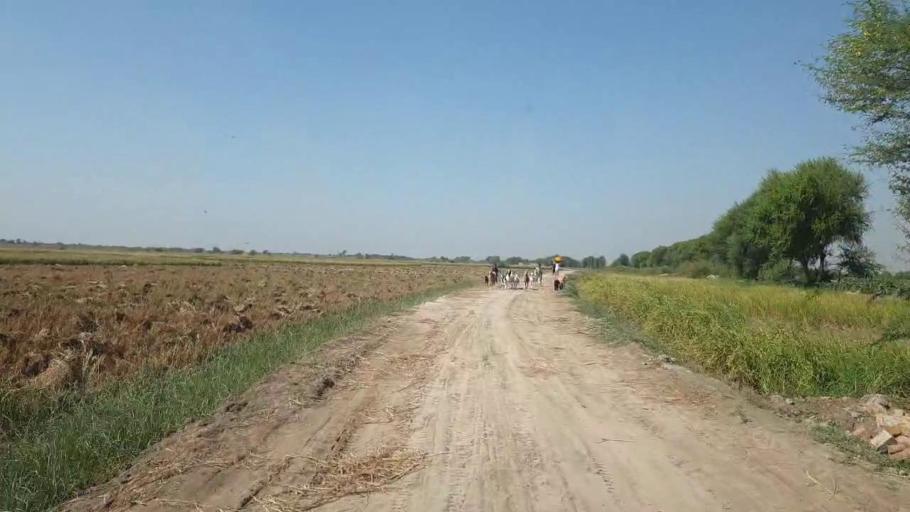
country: PK
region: Sindh
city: Talhar
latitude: 24.8047
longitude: 68.8080
